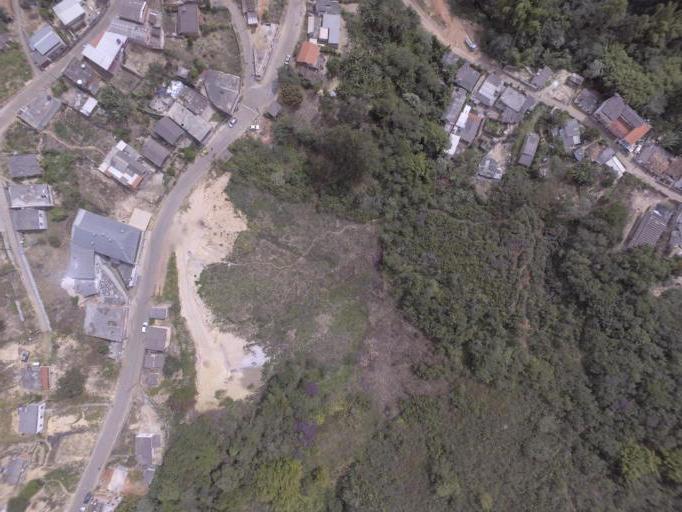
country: BR
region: Minas Gerais
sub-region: Tiradentes
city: Tiradentes
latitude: -21.0544
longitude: -44.0728
